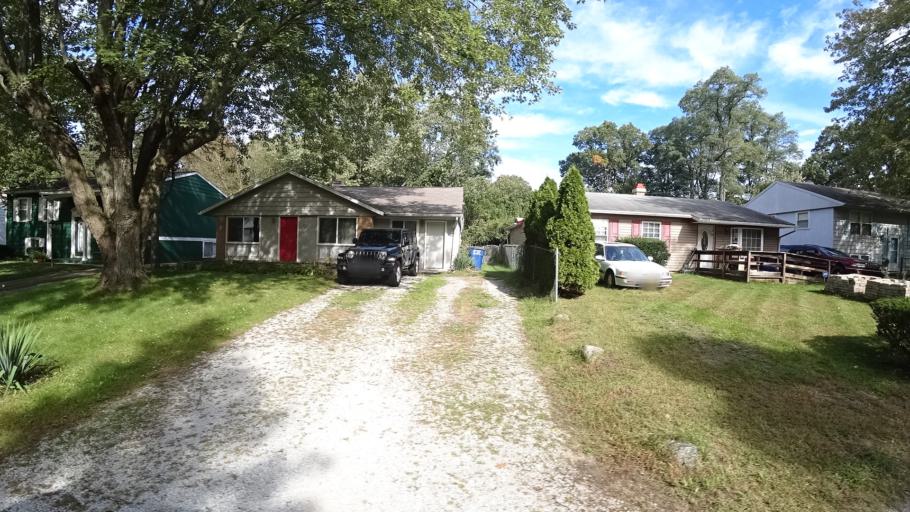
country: US
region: Indiana
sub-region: LaPorte County
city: Michigan City
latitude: 41.7206
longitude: -86.8752
